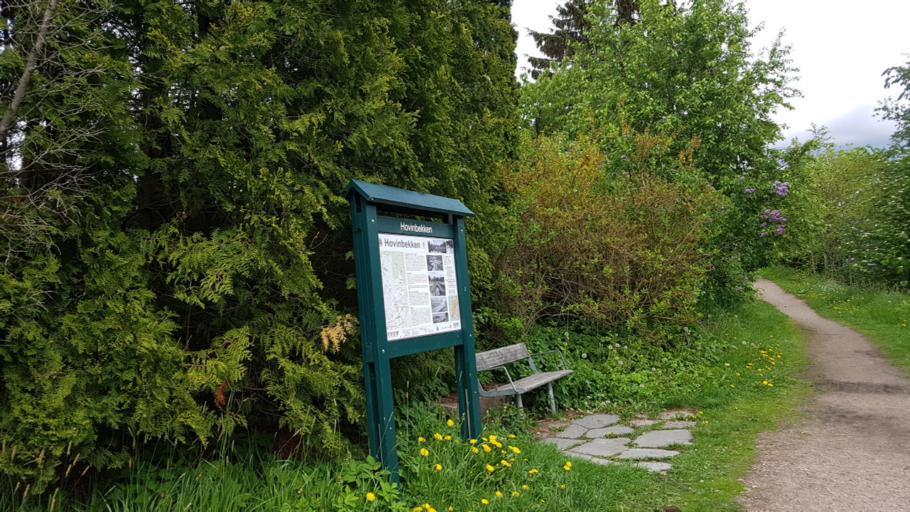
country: NO
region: Oslo
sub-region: Oslo
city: Oslo
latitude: 59.9406
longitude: 10.8225
